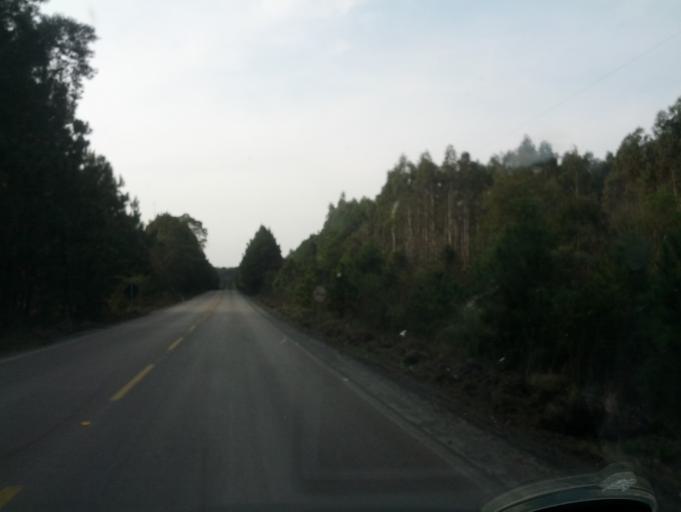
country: BR
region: Santa Catarina
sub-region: Otacilio Costa
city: Otacilio Costa
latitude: -27.3687
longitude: -50.1346
